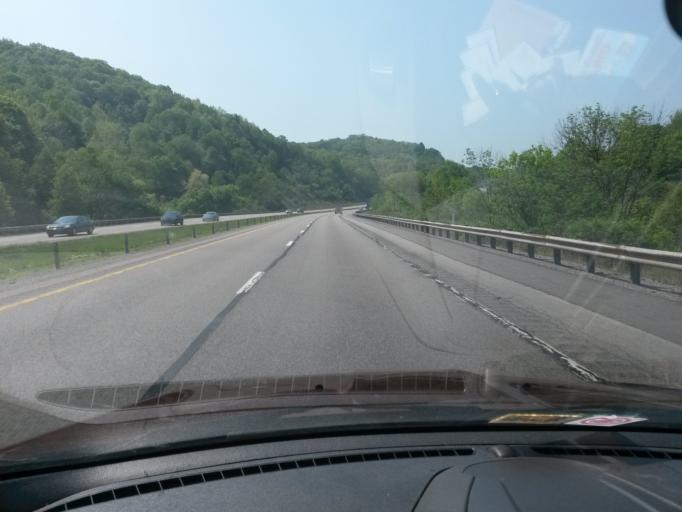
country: US
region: West Virginia
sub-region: Lewis County
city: Weston
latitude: 38.9753
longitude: -80.5115
